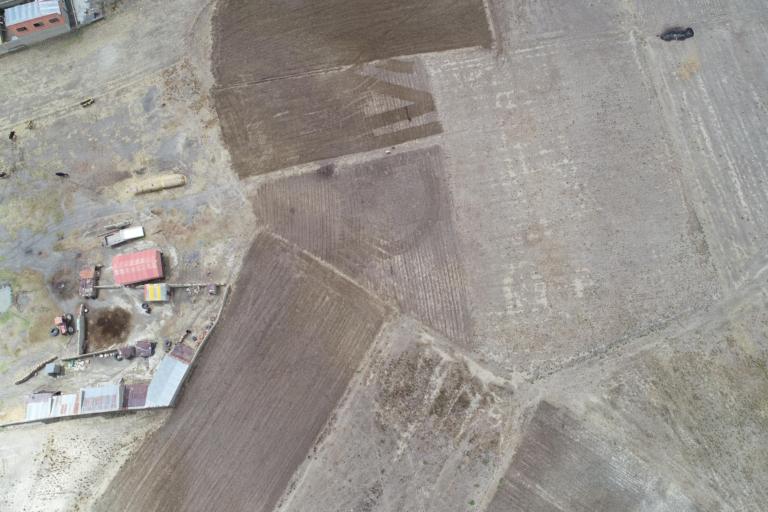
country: BO
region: La Paz
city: Achacachi
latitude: -16.0317
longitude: -68.6910
